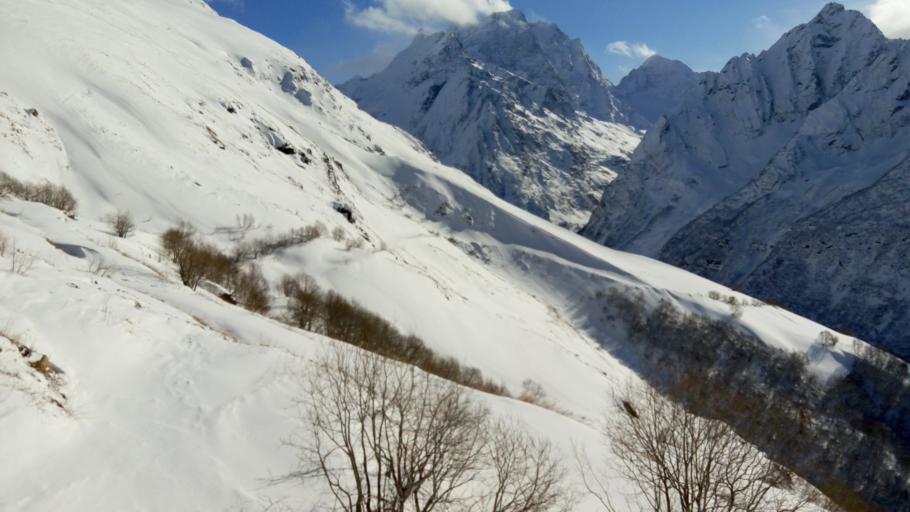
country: RU
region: Karachayevo-Cherkesiya
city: Teberda
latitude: 43.2915
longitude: 41.6528
